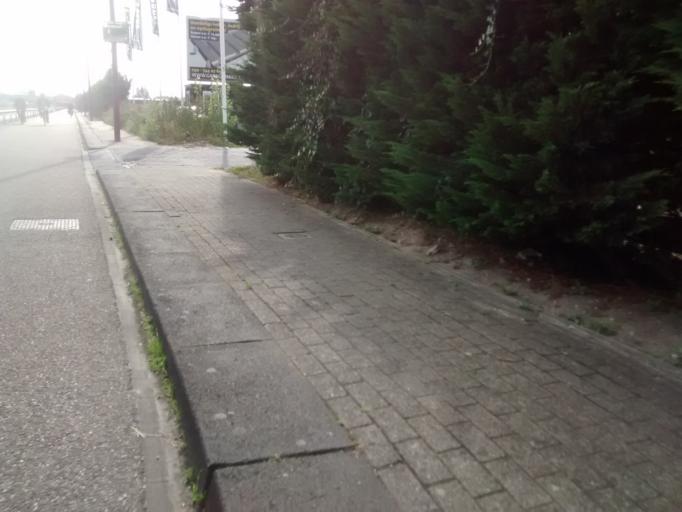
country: NL
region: Utrecht
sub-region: Gemeente Utrecht
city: Lunetten
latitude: 52.0538
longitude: 5.1114
